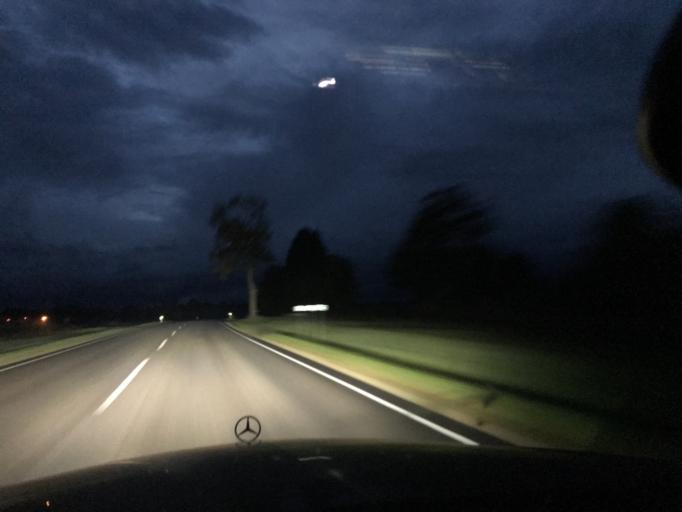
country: EE
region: Valgamaa
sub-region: Torva linn
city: Torva
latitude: 58.0100
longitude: 25.7853
